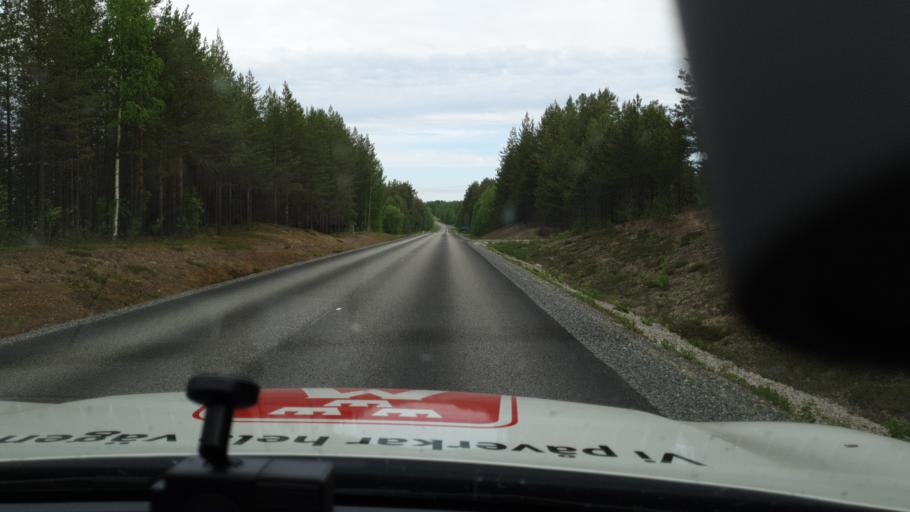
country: SE
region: Vaesterbotten
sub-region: Mala Kommun
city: Mala
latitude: 64.8955
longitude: 18.7119
